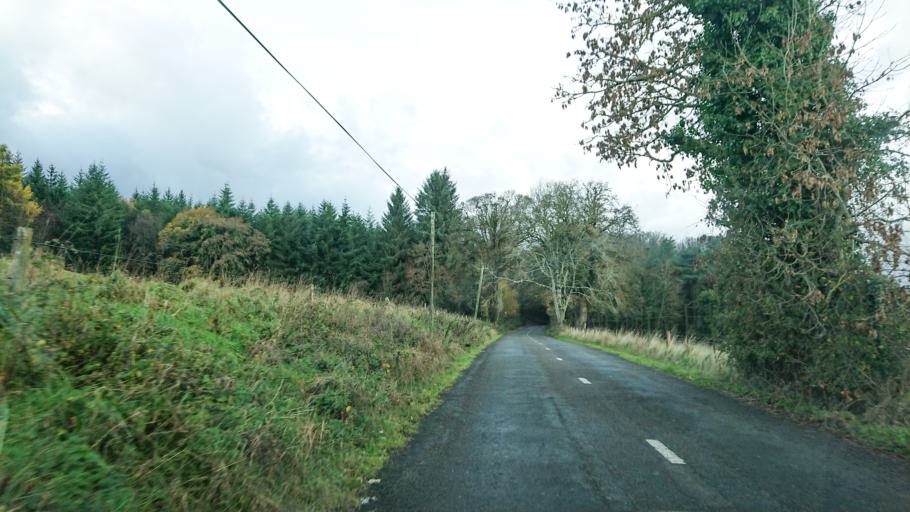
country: IE
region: Munster
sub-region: South Tipperary
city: Cluain Meala
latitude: 52.3565
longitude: -7.5845
